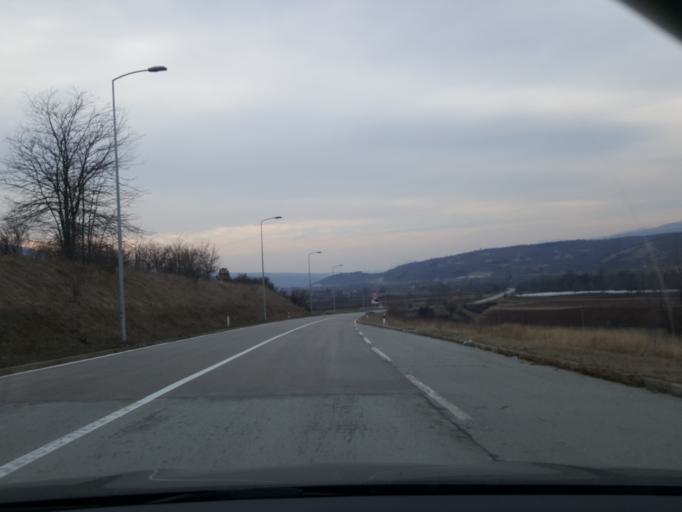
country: RS
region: Central Serbia
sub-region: Pirotski Okrug
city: Bela Palanka
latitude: 43.2218
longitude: 22.3367
